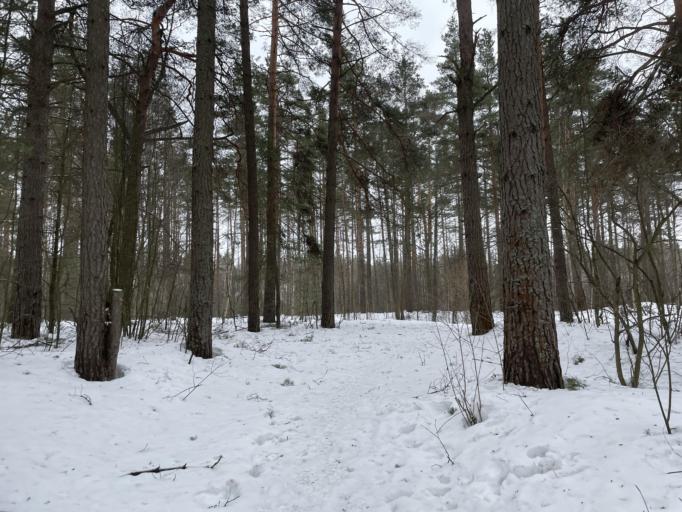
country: RU
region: Vladimir
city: Pokrov
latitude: 55.9444
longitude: 39.2411
